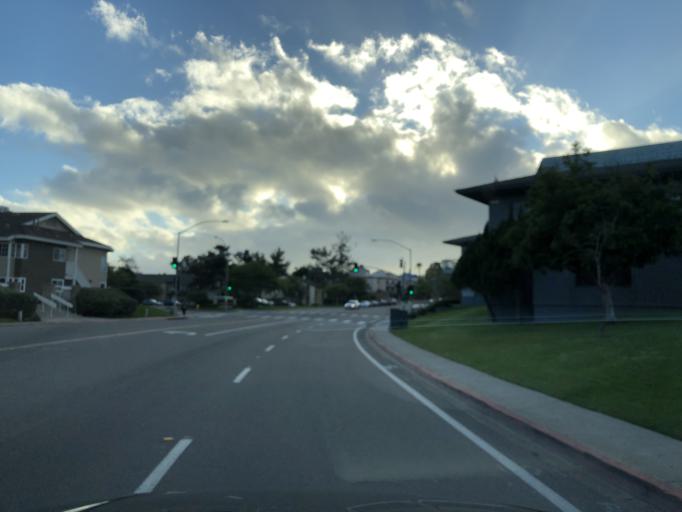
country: US
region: California
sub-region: San Diego County
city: La Jolla
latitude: 32.8186
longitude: -117.1771
